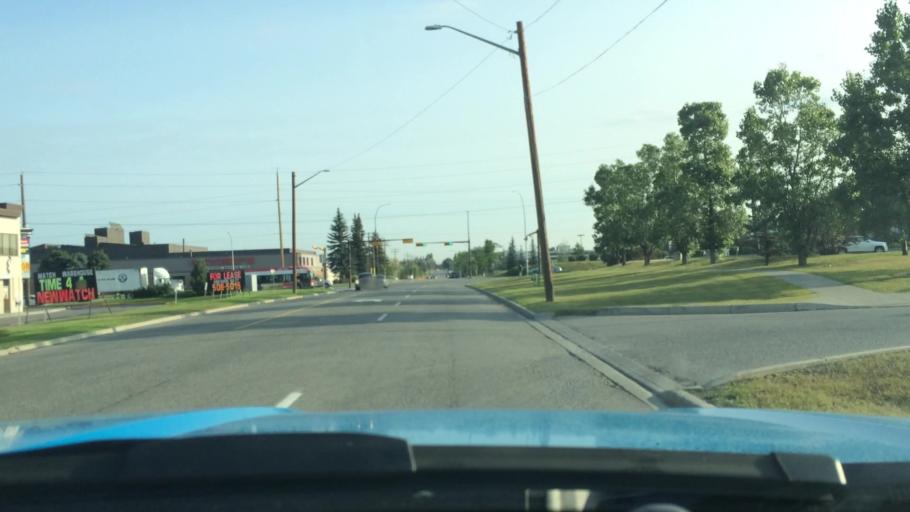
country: CA
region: Alberta
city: Calgary
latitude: 51.0804
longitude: -114.0051
